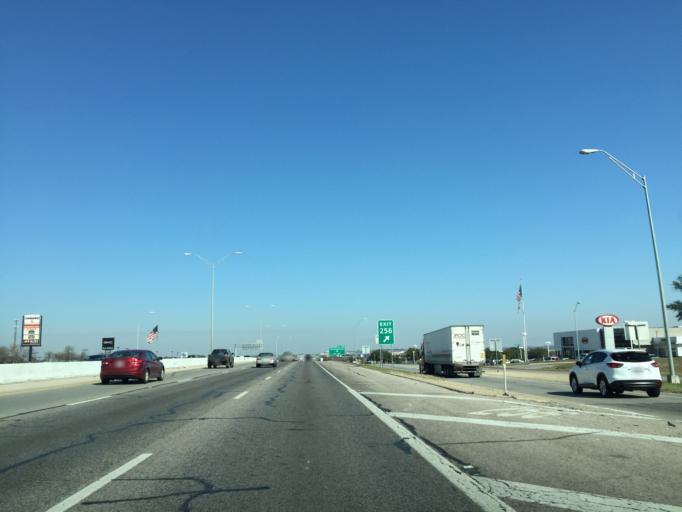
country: US
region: Texas
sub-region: Williamson County
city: Round Rock
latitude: 30.5392
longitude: -97.6921
